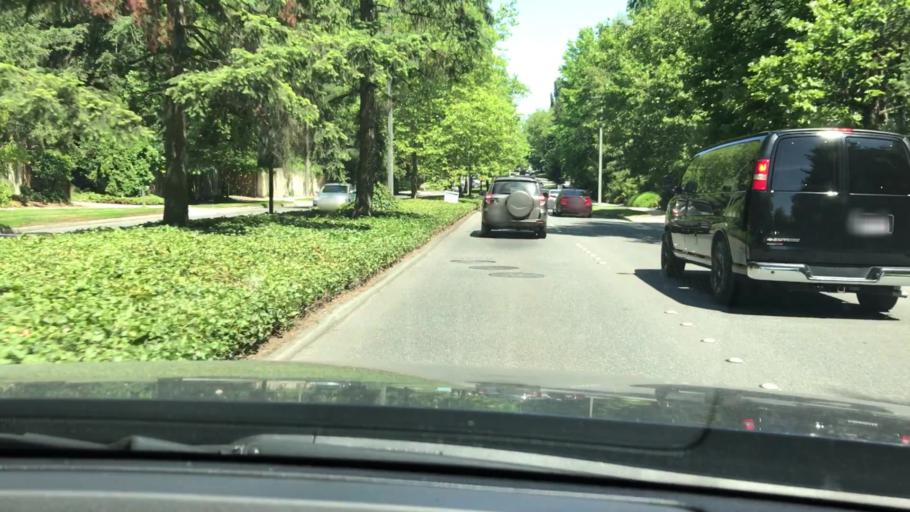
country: US
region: Washington
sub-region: King County
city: Eastgate
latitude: 47.6191
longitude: -122.1431
